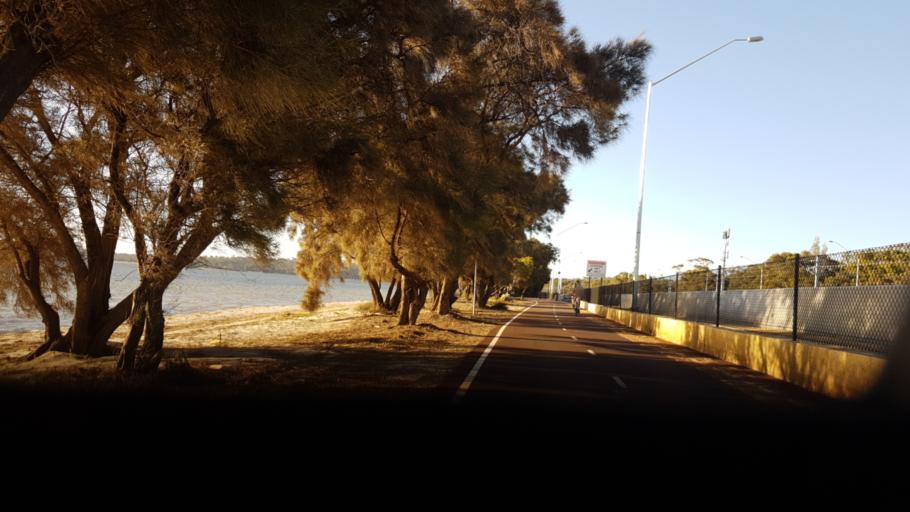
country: AU
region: Western Australia
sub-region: South Perth
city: Como
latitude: -31.9877
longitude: 115.8525
